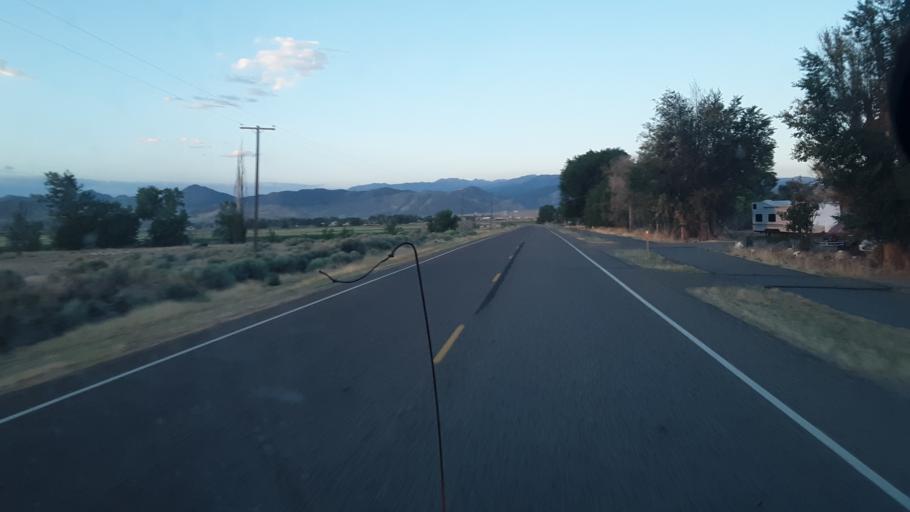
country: US
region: Utah
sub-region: Sevier County
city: Monroe
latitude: 38.6441
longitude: -112.2135
